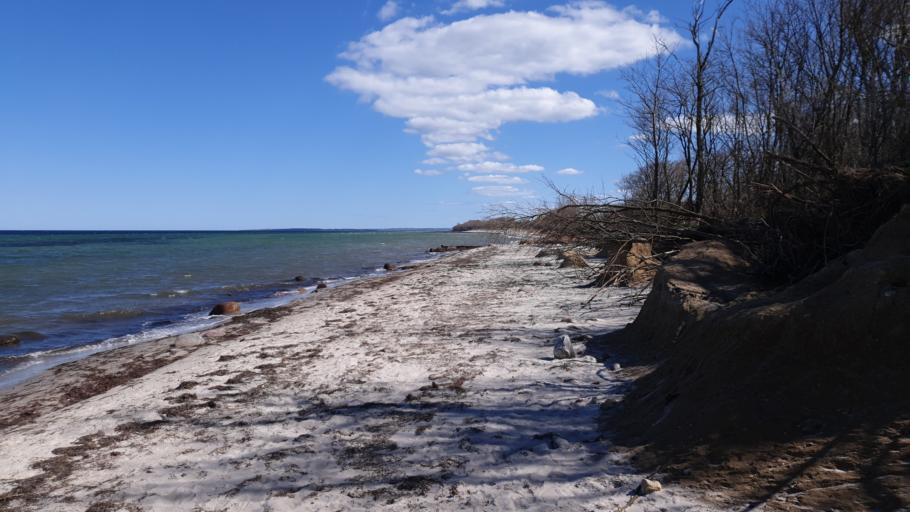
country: DE
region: Mecklenburg-Vorpommern
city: Gramkow
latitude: 54.0089
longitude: 11.4056
